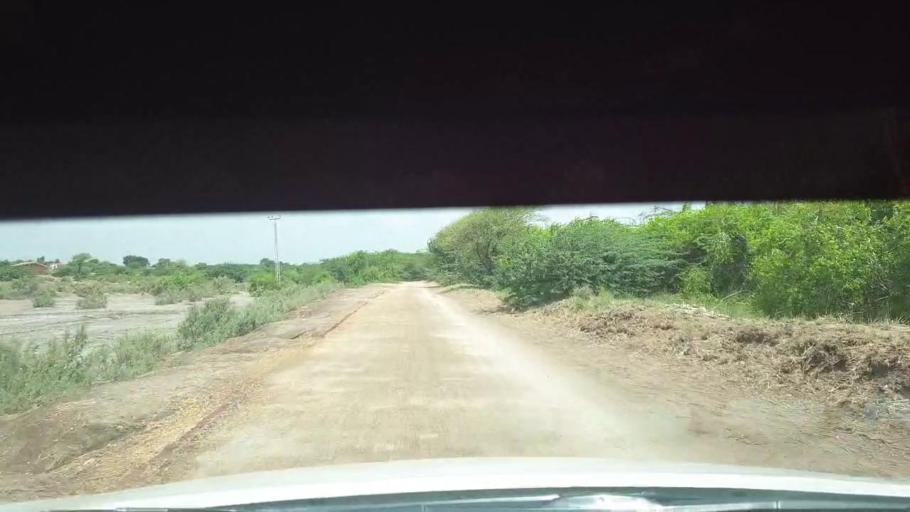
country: PK
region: Sindh
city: Kadhan
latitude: 24.5137
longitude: 68.9744
